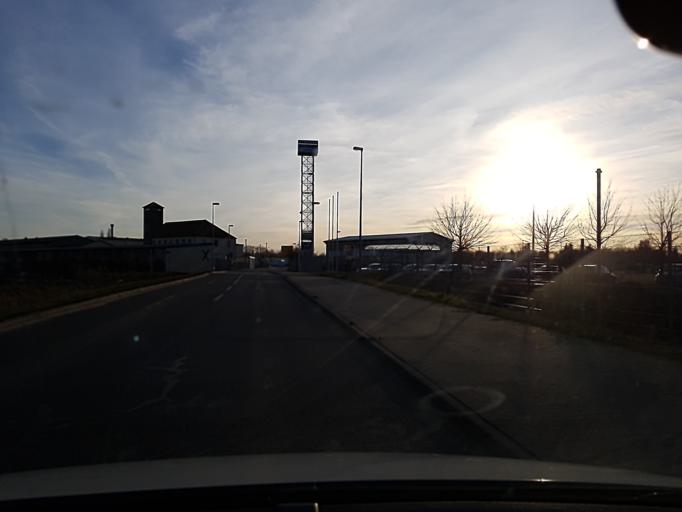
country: DE
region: Brandenburg
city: Finsterwalde
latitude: 51.6346
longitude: 13.7287
